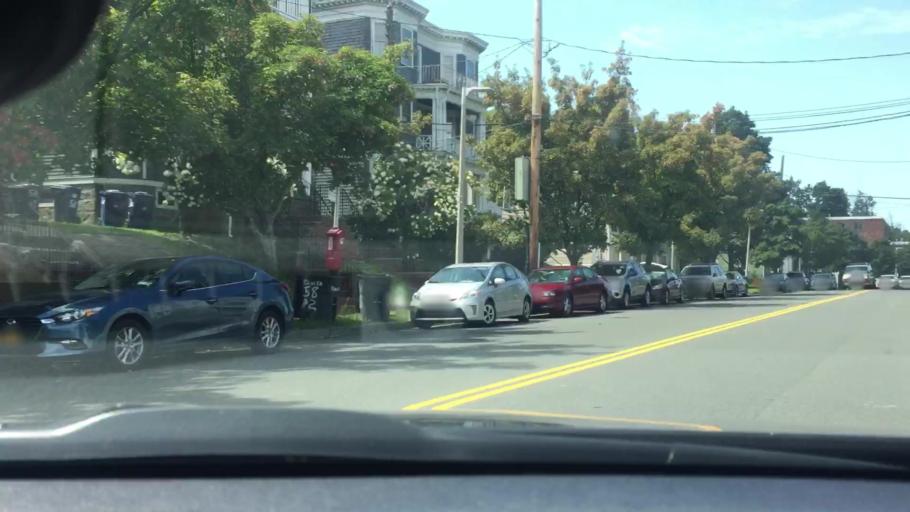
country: US
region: Massachusetts
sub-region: Middlesex County
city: Watertown
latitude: 42.3503
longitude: -71.1706
